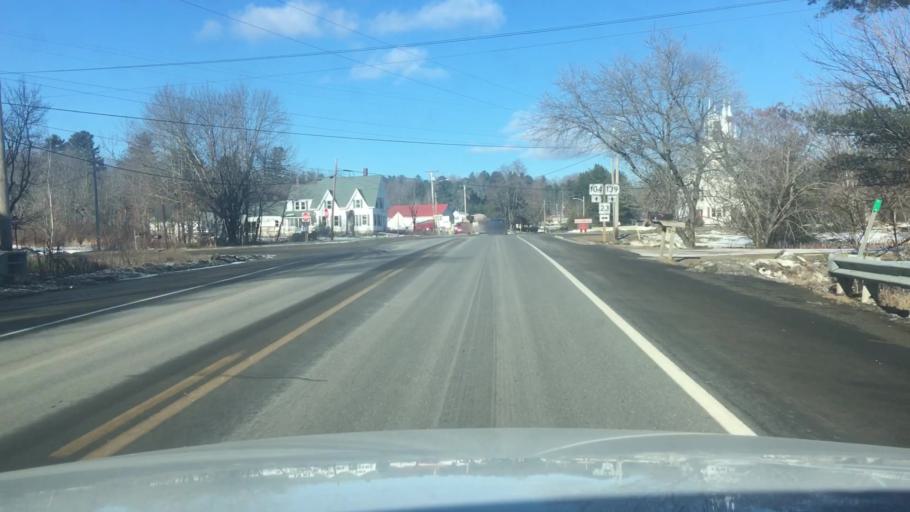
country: US
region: Maine
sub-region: Kennebec County
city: Waterville
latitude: 44.6061
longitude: -69.6619
